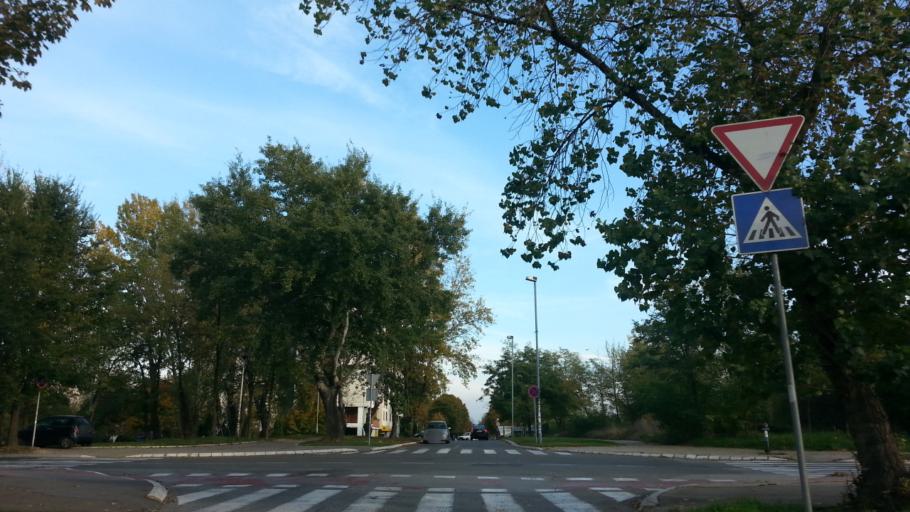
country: RS
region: Central Serbia
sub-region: Belgrade
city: Zemun
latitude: 44.8175
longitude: 20.3763
